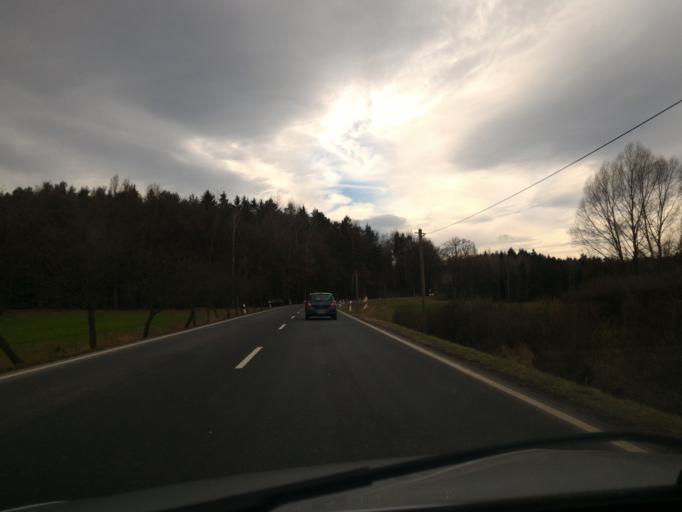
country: DE
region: Saxony
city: Durrrohrsdorf
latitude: 51.0670
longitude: 13.9902
